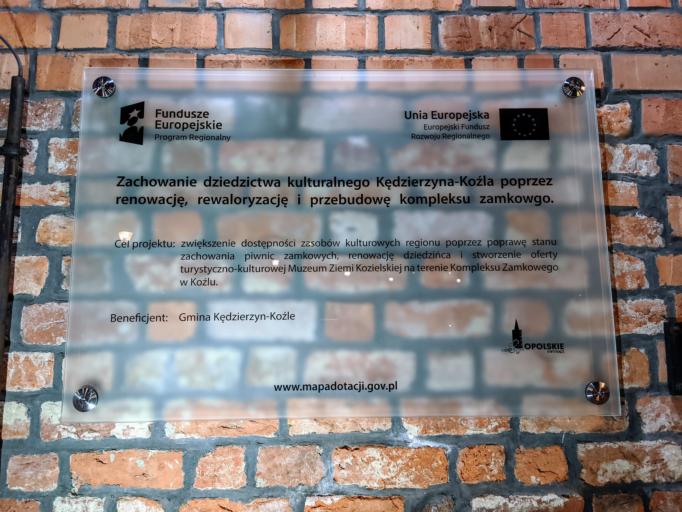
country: PL
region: Opole Voivodeship
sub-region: Powiat kedzierzynsko-kozielski
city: Kozle
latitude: 50.3346
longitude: 18.1426
